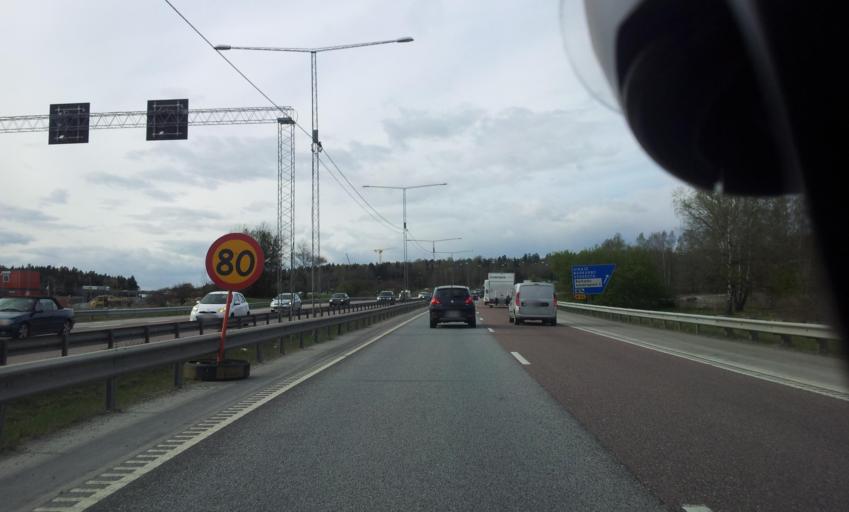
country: SE
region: Stockholm
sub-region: Jarfalla Kommun
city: Jakobsberg
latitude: 59.4079
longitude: 17.8606
